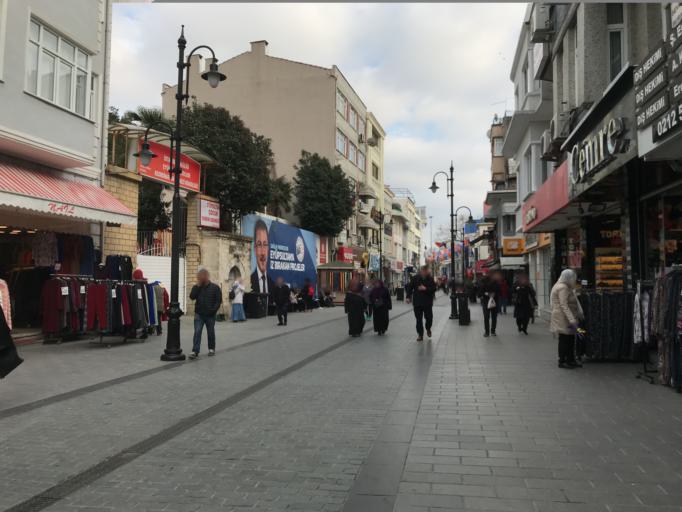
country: TR
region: Istanbul
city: Istanbul
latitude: 41.0490
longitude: 28.9312
